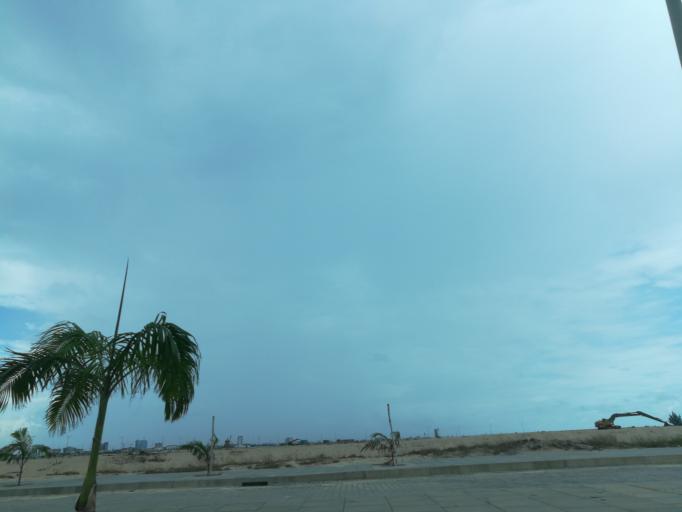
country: NG
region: Lagos
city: Ikoyi
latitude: 6.4085
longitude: 3.4204
